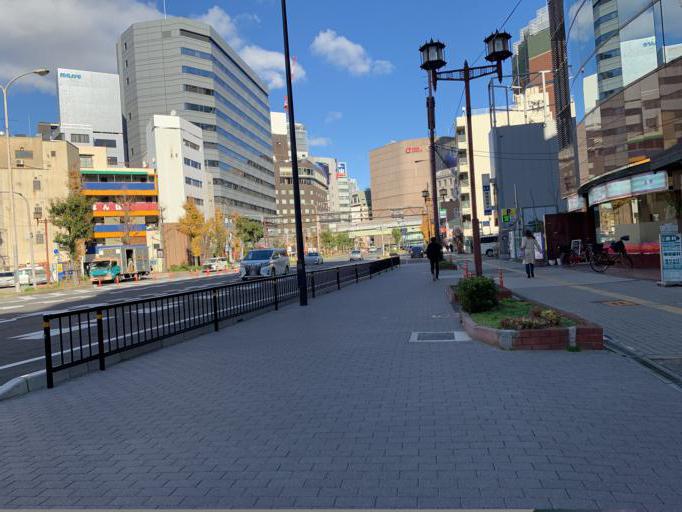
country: JP
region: Osaka
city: Osaka-shi
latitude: 34.6633
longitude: 135.4985
